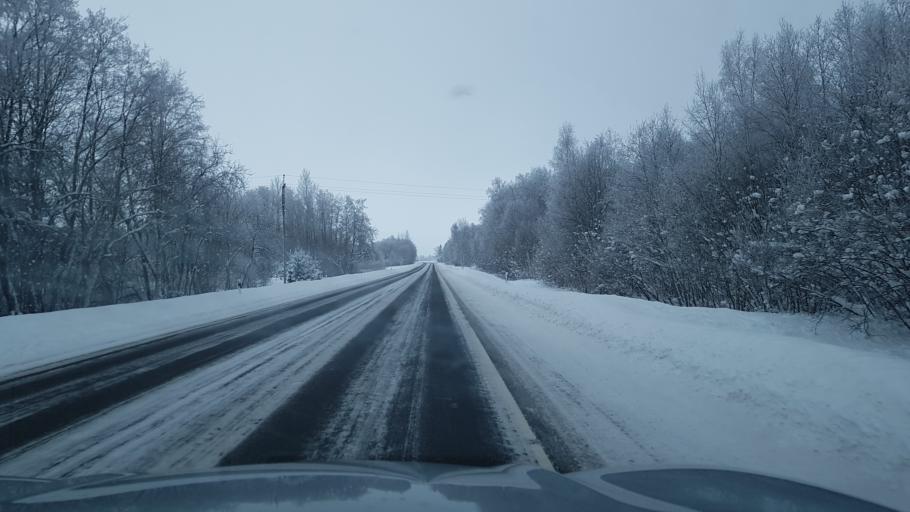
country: EE
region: Ida-Virumaa
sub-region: Johvi vald
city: Johvi
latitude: 59.2775
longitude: 27.3907
